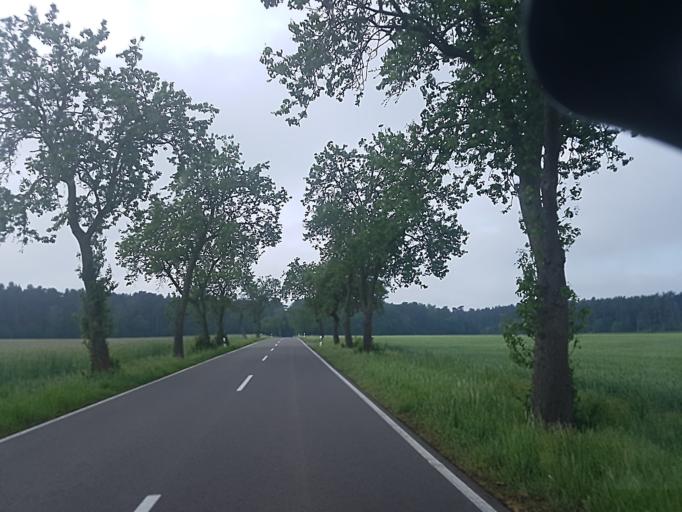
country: DE
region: Saxony-Anhalt
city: Klieken
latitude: 52.0032
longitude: 12.3697
